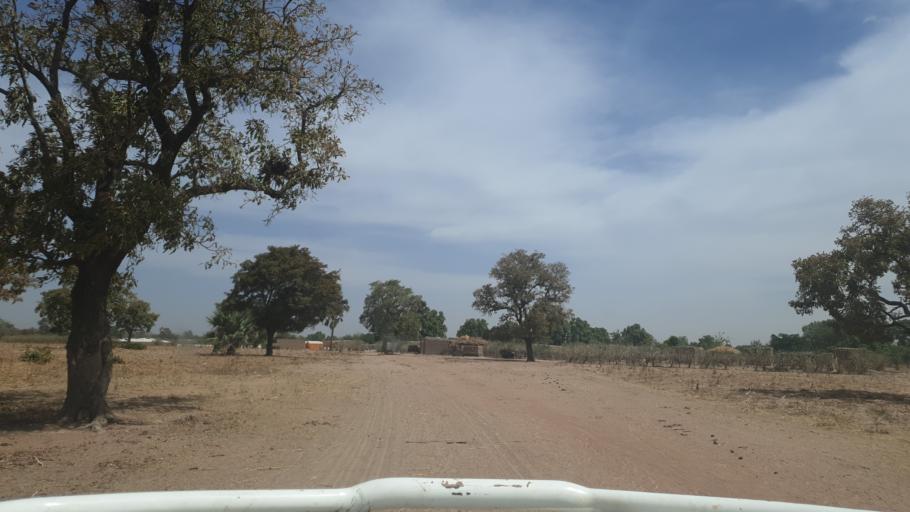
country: ML
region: Sikasso
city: Yorosso
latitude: 12.2762
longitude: -4.6897
